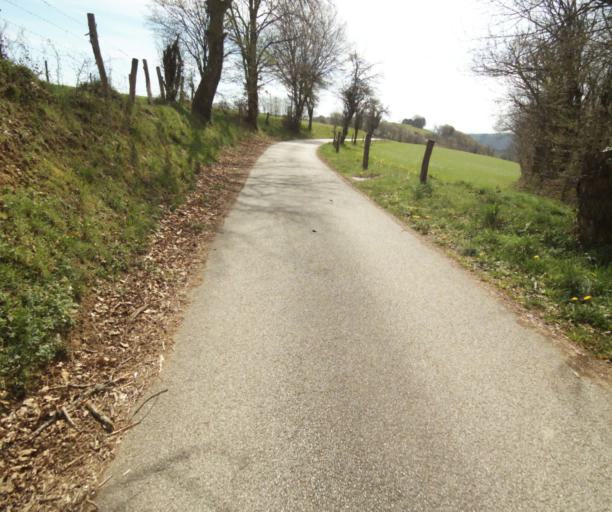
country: FR
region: Limousin
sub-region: Departement de la Correze
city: Naves
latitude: 45.3567
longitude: 1.7970
